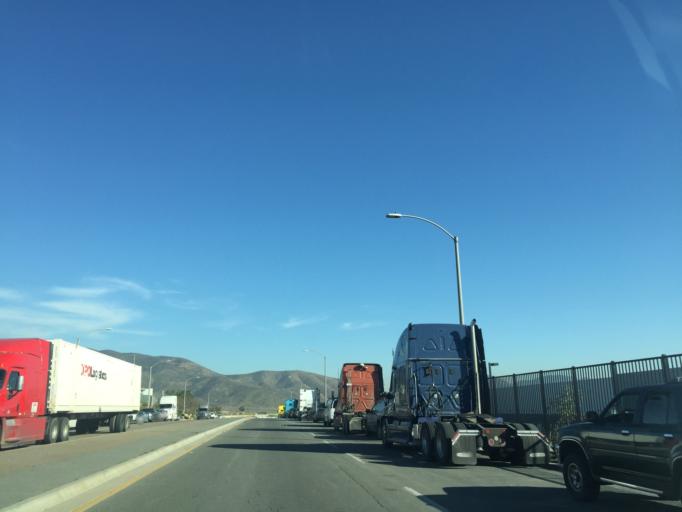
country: MX
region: Baja California
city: Tijuana
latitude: 32.5599
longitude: -116.9265
